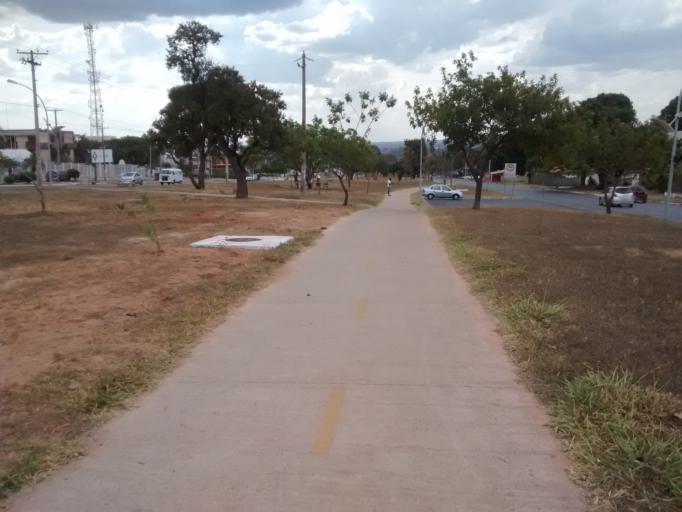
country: BR
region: Federal District
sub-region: Brasilia
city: Brasilia
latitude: -15.7481
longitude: -47.8993
